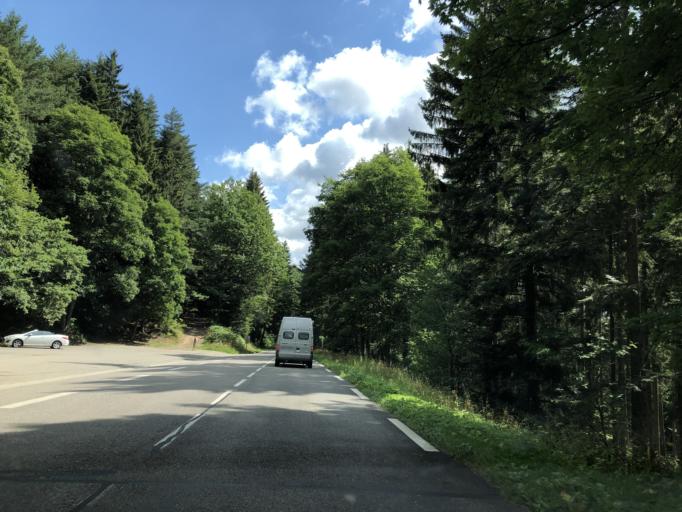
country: FR
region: Alsace
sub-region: Departement du Haut-Rhin
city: Soultzeren
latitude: 48.0637
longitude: 7.0654
